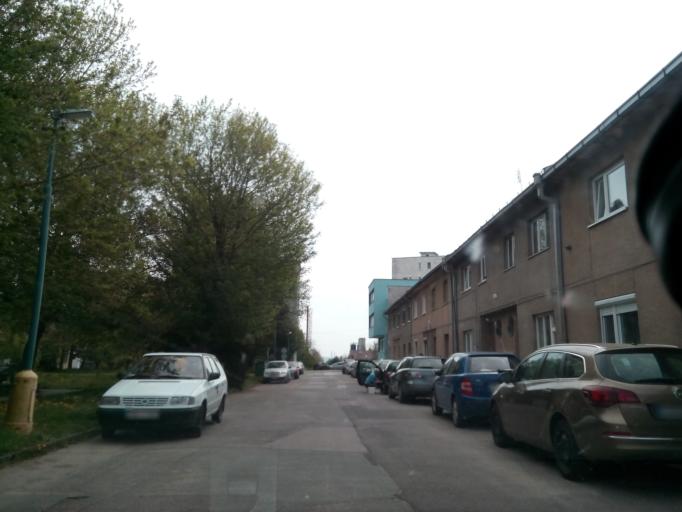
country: SK
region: Trnavsky
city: Vrbove
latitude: 48.6210
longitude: 17.7279
